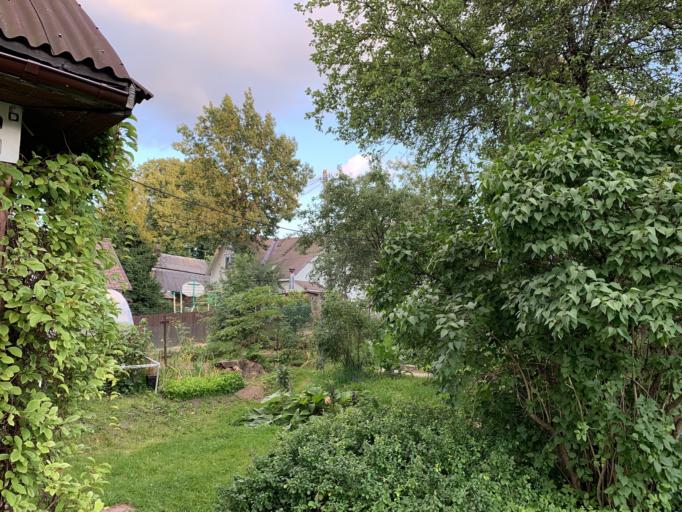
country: RU
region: St.-Petersburg
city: Pargolovo
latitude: 60.0794
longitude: 30.2738
